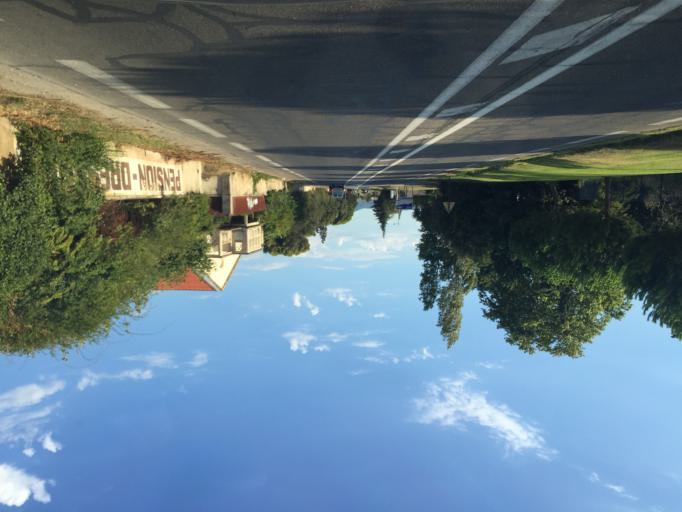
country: FR
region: Provence-Alpes-Cote d'Azur
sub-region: Departement du Vaucluse
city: Carpentras
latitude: 44.0254
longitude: 5.0523
